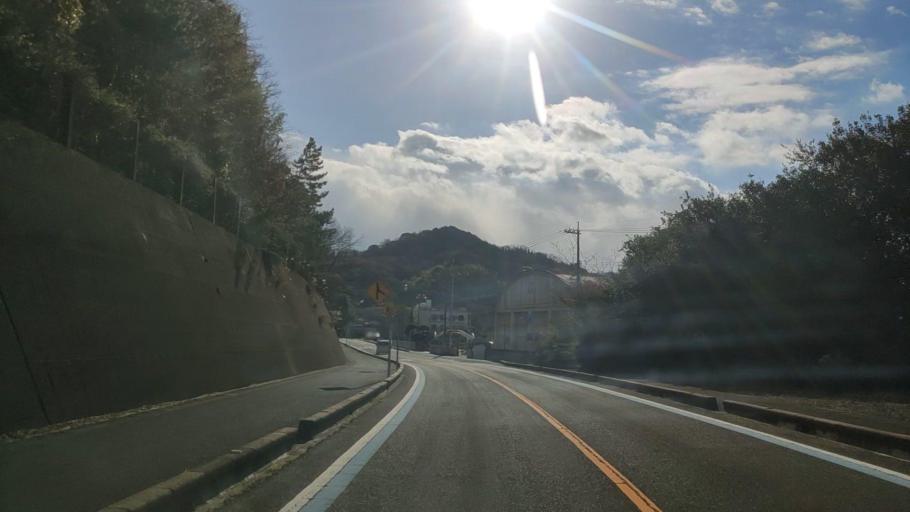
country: JP
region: Hiroshima
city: Innoshima
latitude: 34.2190
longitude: 133.0679
